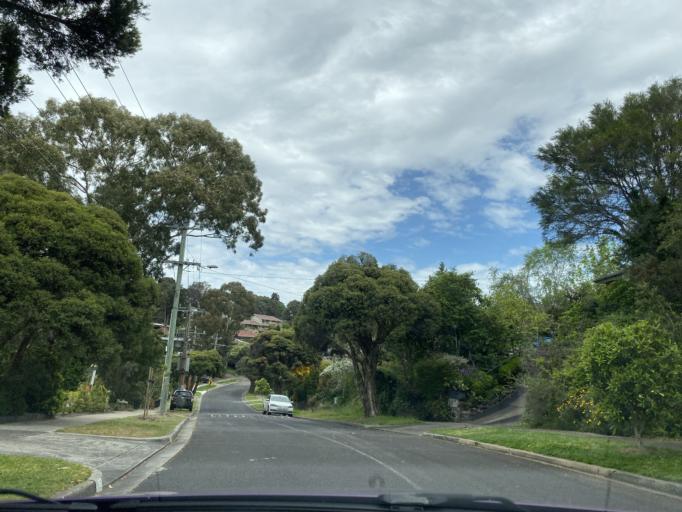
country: AU
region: Victoria
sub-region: Manningham
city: Templestowe Lower
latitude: -37.7640
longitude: 145.1250
